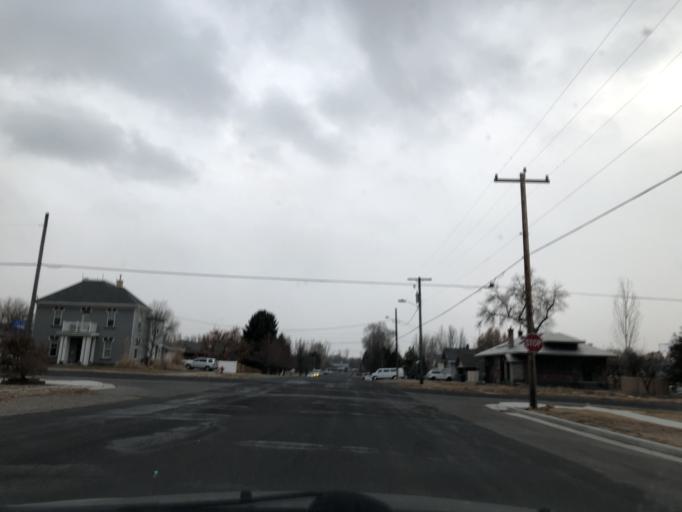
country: US
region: Utah
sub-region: Cache County
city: Logan
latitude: 41.7282
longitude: -111.8480
